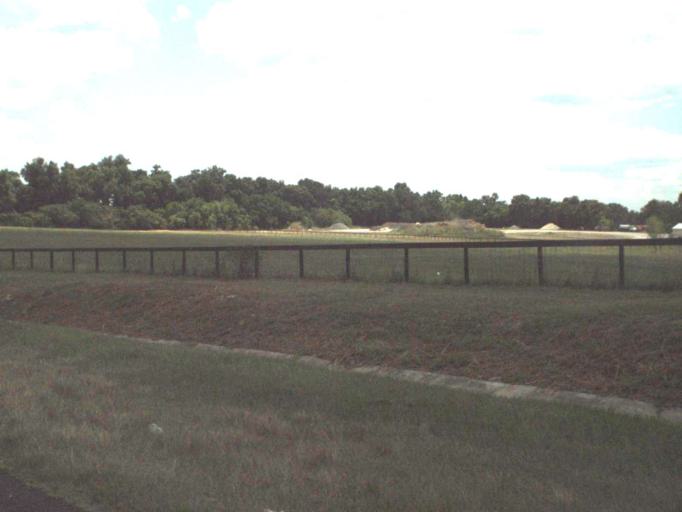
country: US
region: Florida
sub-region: Marion County
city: Ocala
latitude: 29.2954
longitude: -82.1520
